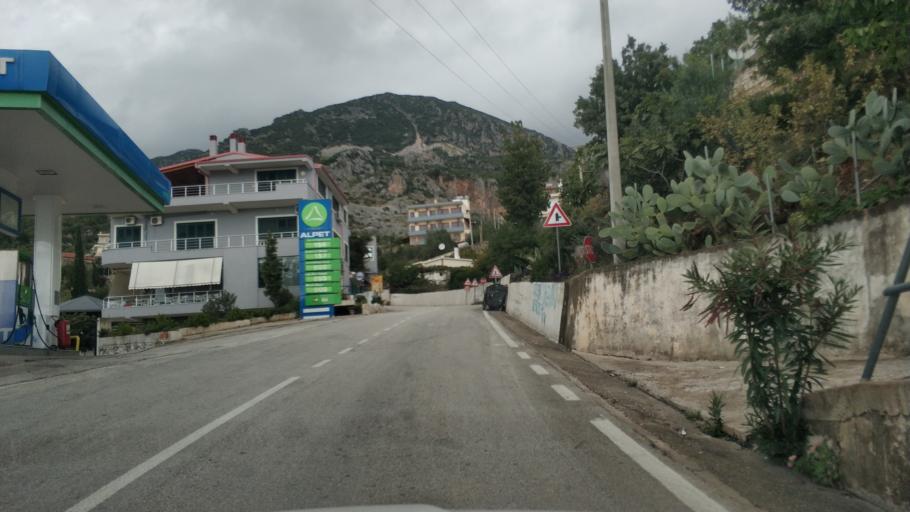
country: AL
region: Vlore
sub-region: Rrethi i Vlores
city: Vranisht
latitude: 40.1553
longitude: 19.6331
